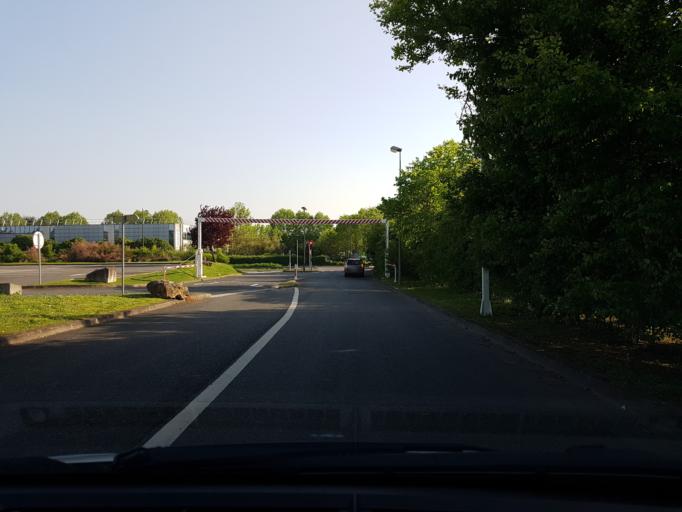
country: FR
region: Ile-de-France
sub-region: Departement du Val-de-Marne
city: Fresnes
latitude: 48.7547
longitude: 2.3382
